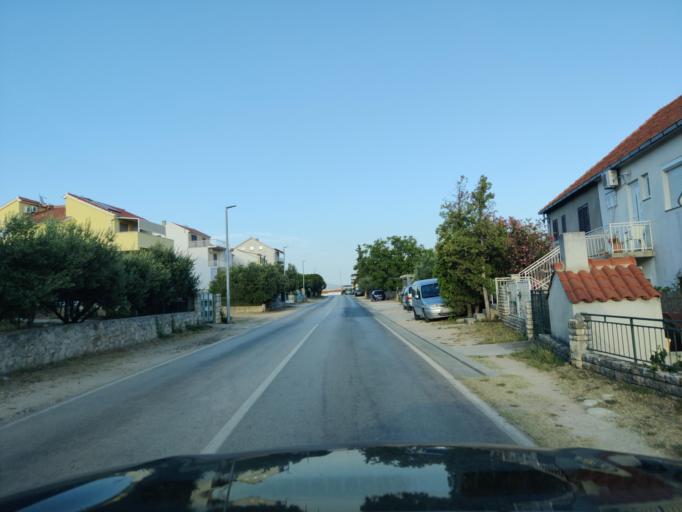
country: HR
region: Sibensko-Kniniska
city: Vodice
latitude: 43.7580
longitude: 15.7655
